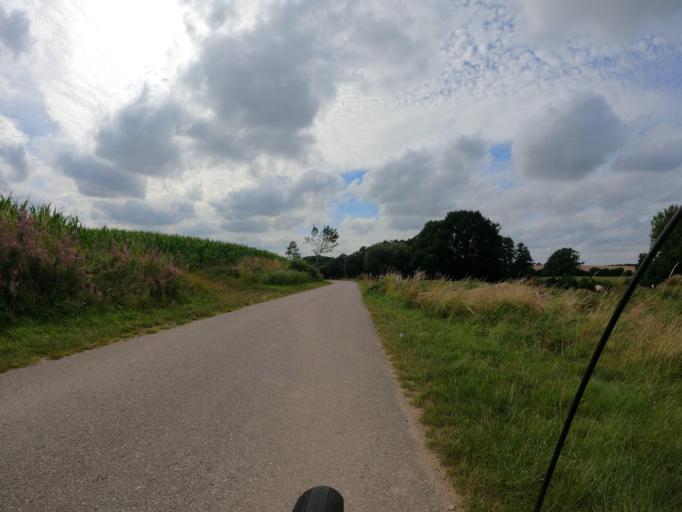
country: DE
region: Schleswig-Holstein
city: Niesgrau
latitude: 54.7463
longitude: 9.8065
